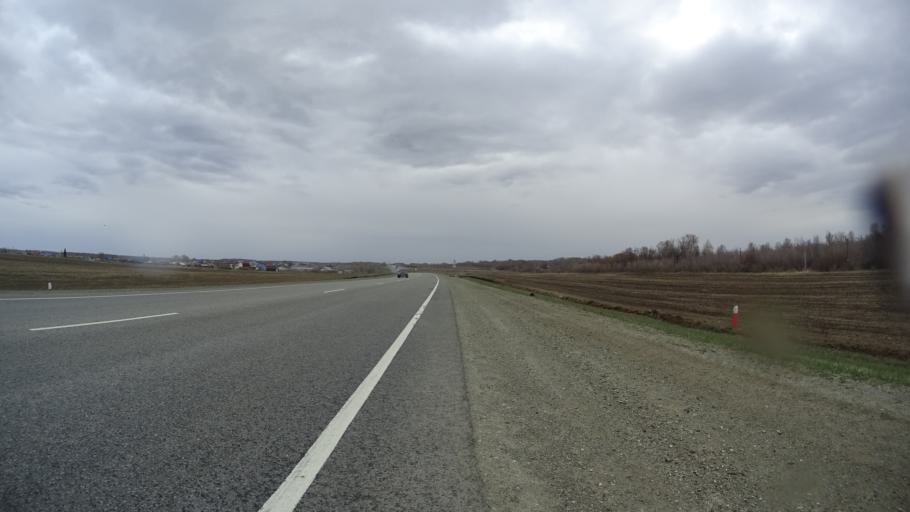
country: RU
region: Chelyabinsk
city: Krasnogorskiy
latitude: 54.6795
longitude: 61.2471
